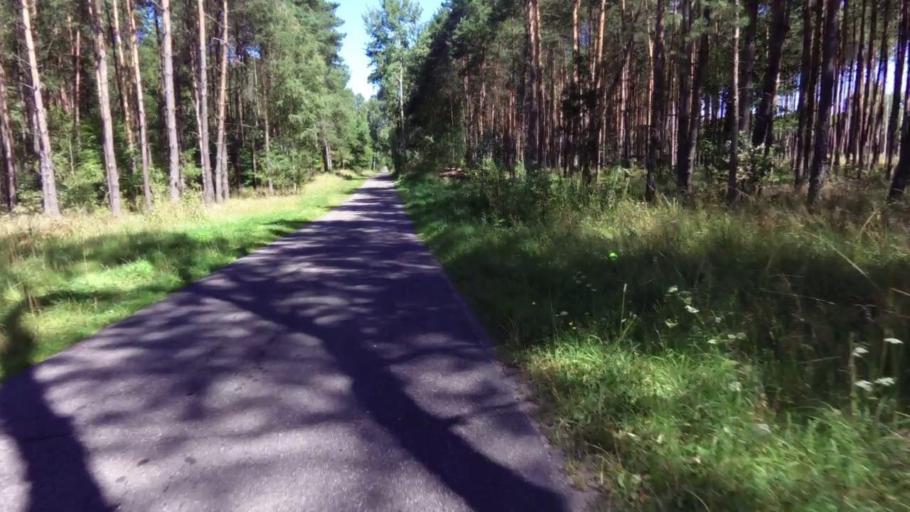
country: PL
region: West Pomeranian Voivodeship
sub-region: Powiat szczecinecki
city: Lubowo
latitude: 53.5756
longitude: 16.3693
